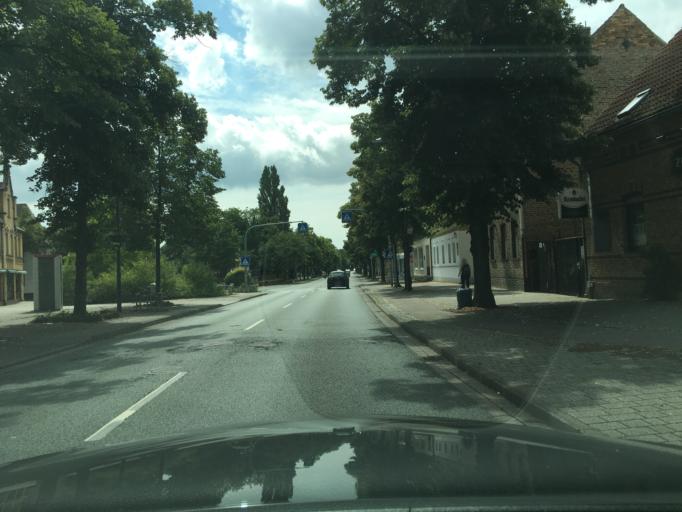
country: DE
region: Saxony-Anhalt
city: Wolfen
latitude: 51.6616
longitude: 12.2760
